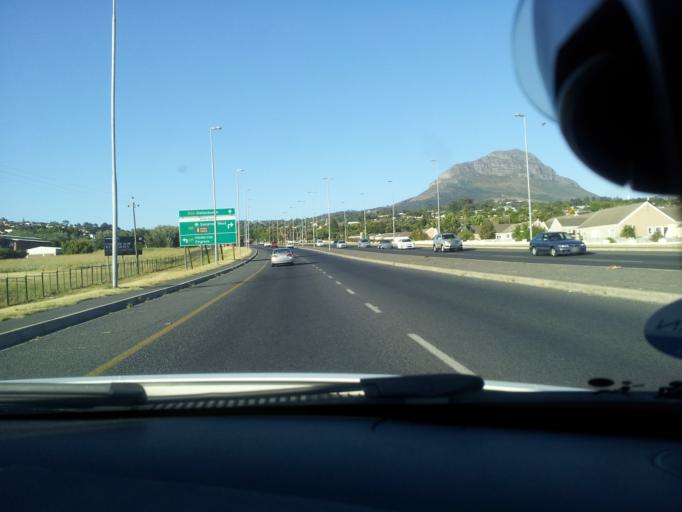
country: ZA
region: Western Cape
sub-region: Cape Winelands District Municipality
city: Stellenbosch
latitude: -34.0724
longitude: 18.8238
